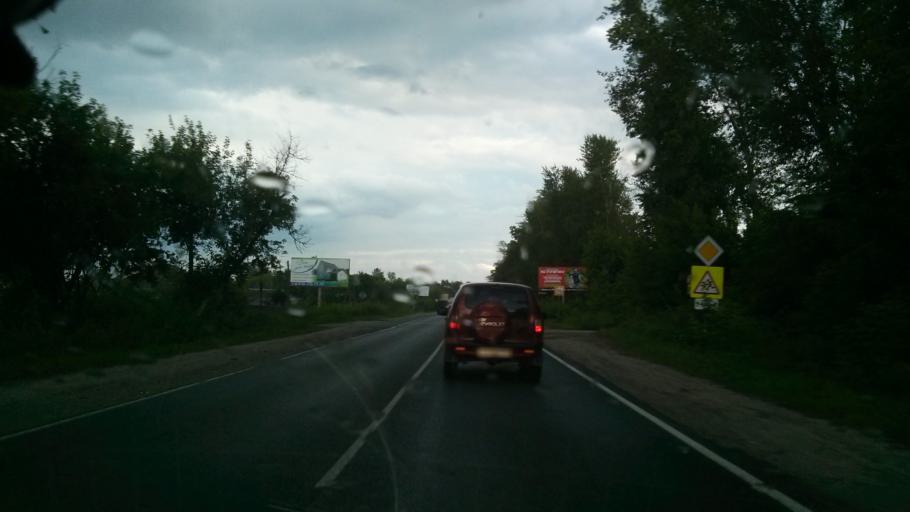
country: RU
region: Vladimir
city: Murom
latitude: 55.6025
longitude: 42.0294
